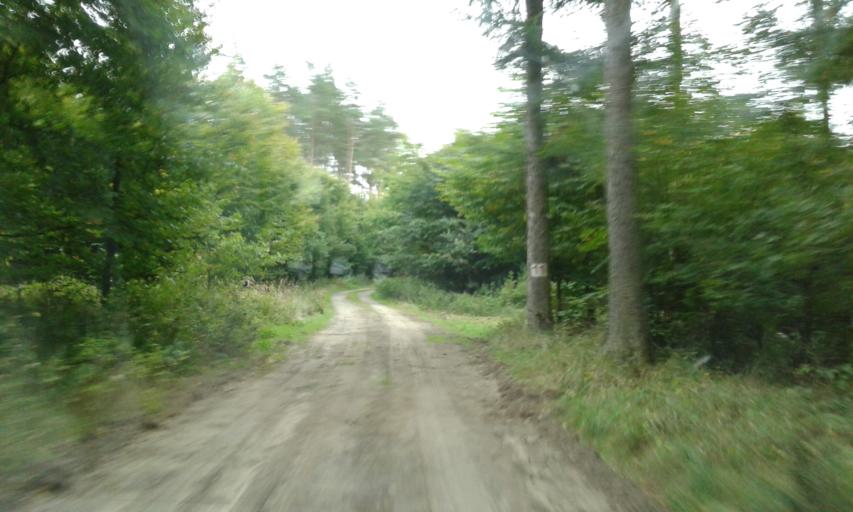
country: PL
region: West Pomeranian Voivodeship
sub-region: Powiat choszczenski
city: Pelczyce
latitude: 53.0894
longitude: 15.2472
